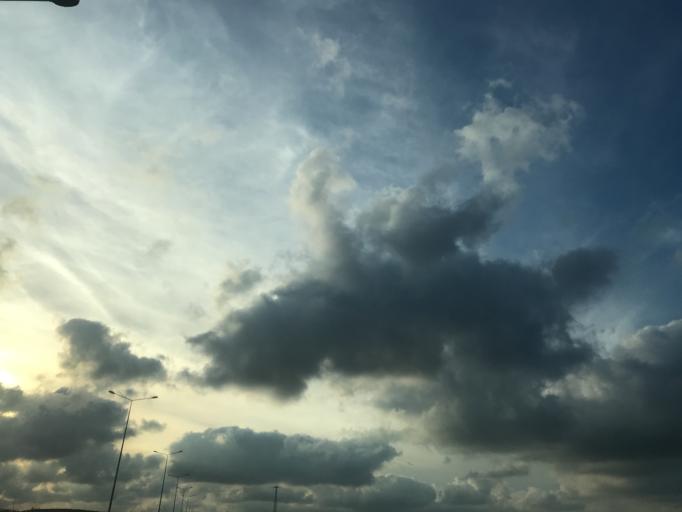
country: TR
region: Istanbul
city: Kemerburgaz
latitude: 41.2398
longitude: 28.8034
